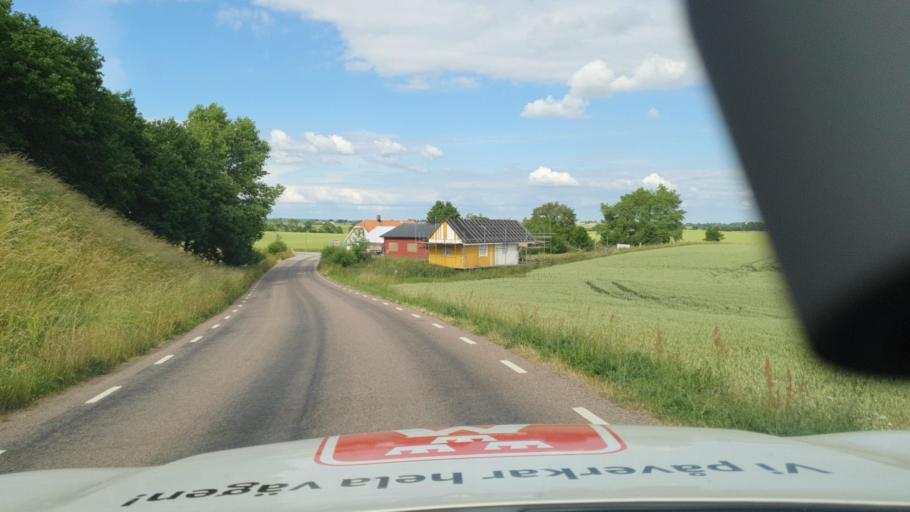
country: SE
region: Skane
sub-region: Skurups Kommun
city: Skurup
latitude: 55.4458
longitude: 13.4734
